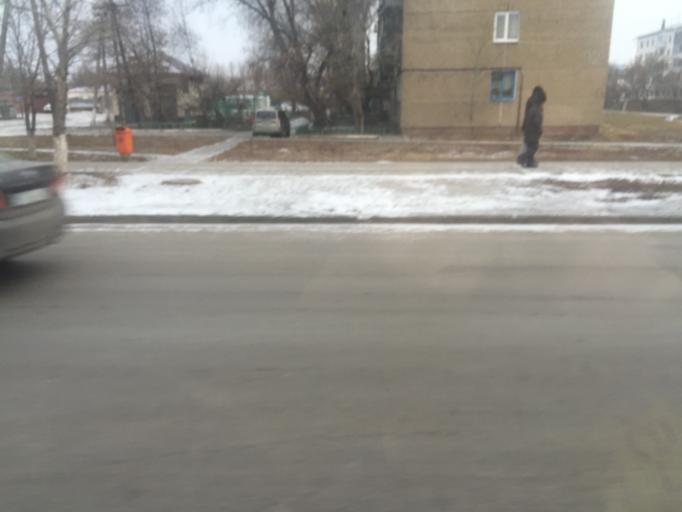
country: KZ
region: Astana Qalasy
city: Astana
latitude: 51.1937
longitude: 71.4008
